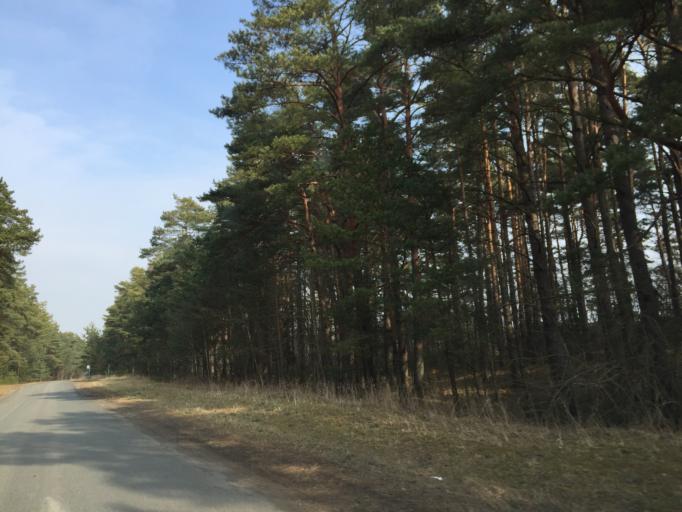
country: LV
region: Salacgrivas
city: Ainazi
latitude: 57.8887
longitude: 24.3685
